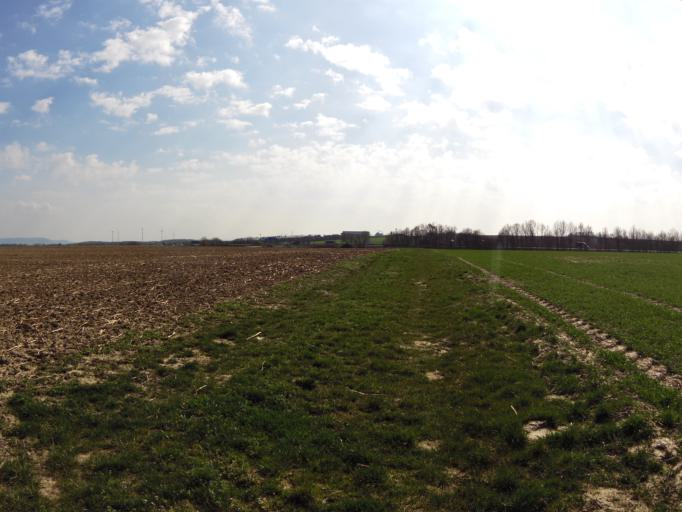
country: DE
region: Bavaria
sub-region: Regierungsbezirk Unterfranken
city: Rottendorf
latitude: 49.7949
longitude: 10.0613
